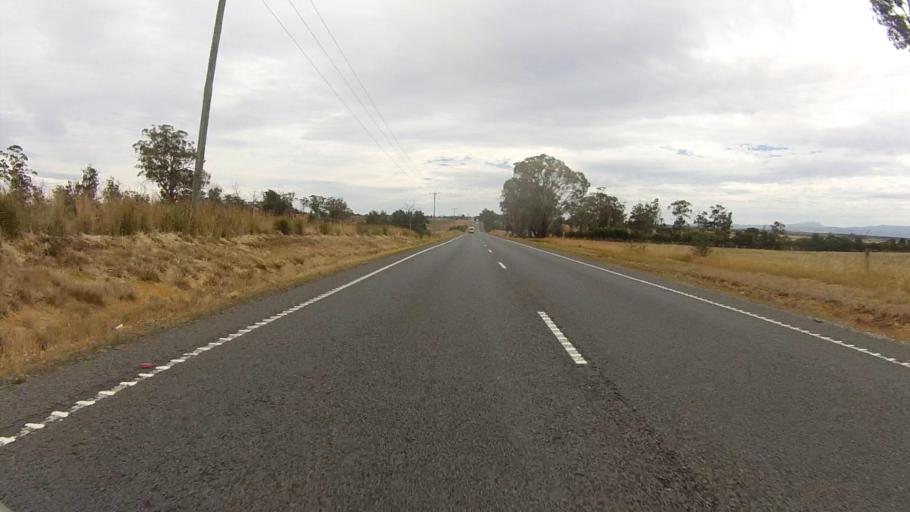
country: AU
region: Tasmania
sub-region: Northern Midlands
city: Evandale
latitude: -41.7047
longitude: 147.2958
